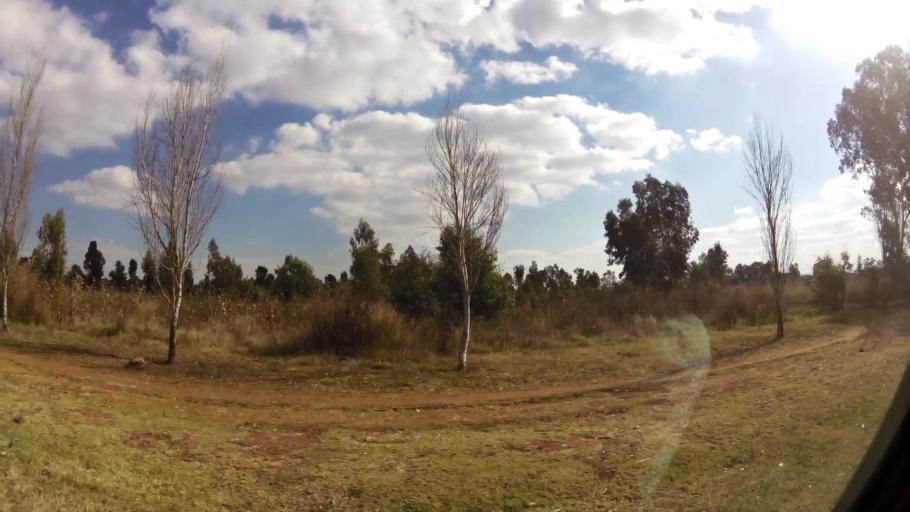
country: ZA
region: Gauteng
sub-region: Ekurhuleni Metropolitan Municipality
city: Tembisa
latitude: -25.9773
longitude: 28.2401
